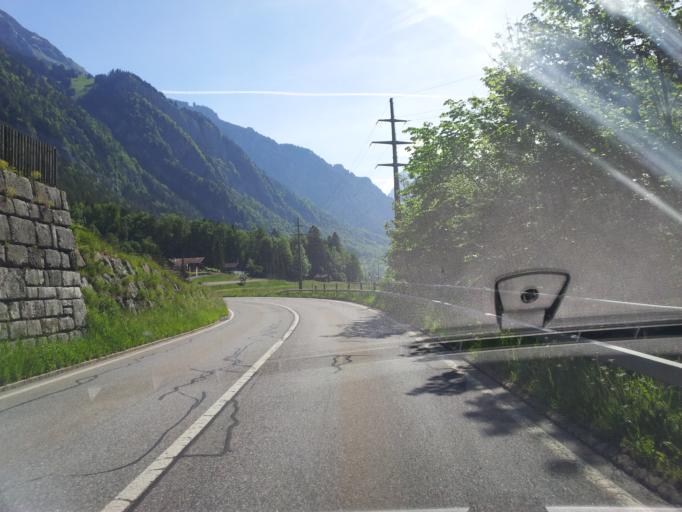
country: CH
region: Bern
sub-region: Interlaken-Oberhasli District
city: Lauterbrunnen
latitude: 46.6357
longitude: 7.9224
